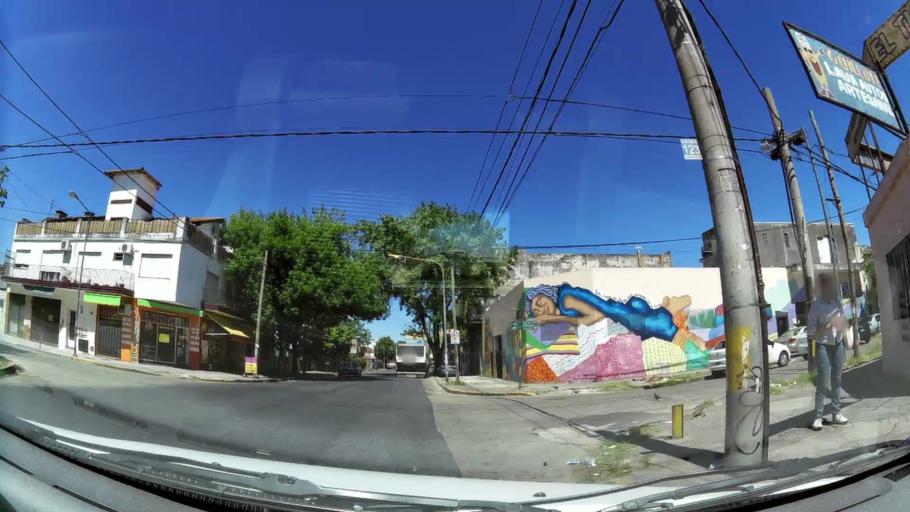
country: AR
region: Buenos Aires
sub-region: Partido de General San Martin
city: General San Martin
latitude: -34.5925
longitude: -58.5344
